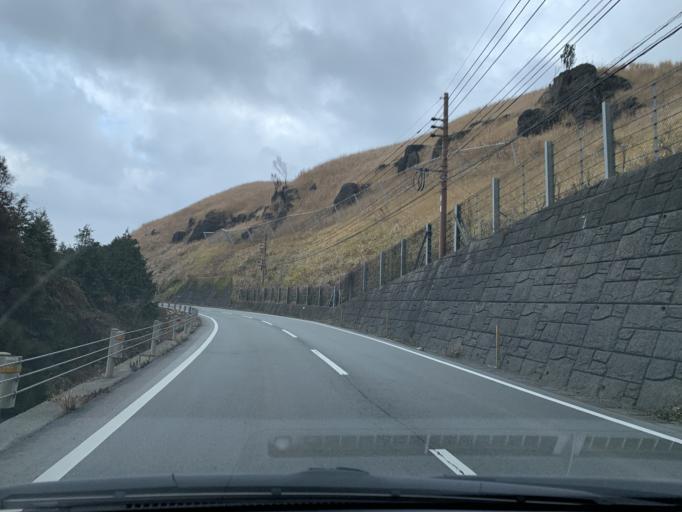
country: JP
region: Kumamoto
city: Ozu
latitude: 32.9137
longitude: 130.9688
